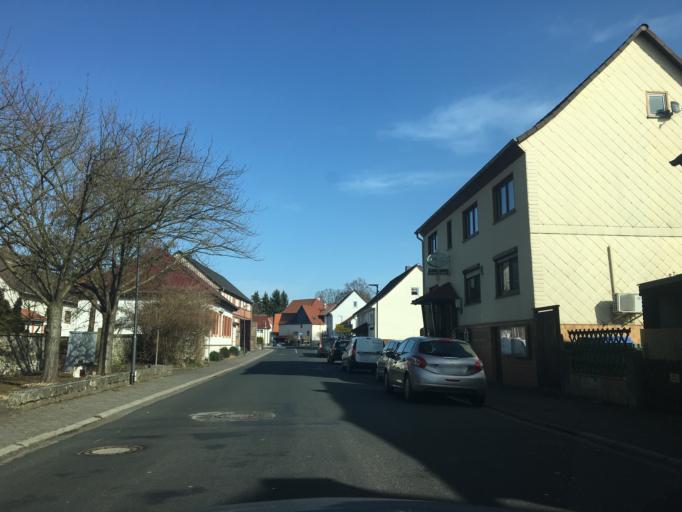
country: DE
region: Hesse
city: Romrod
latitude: 50.7136
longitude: 9.2207
